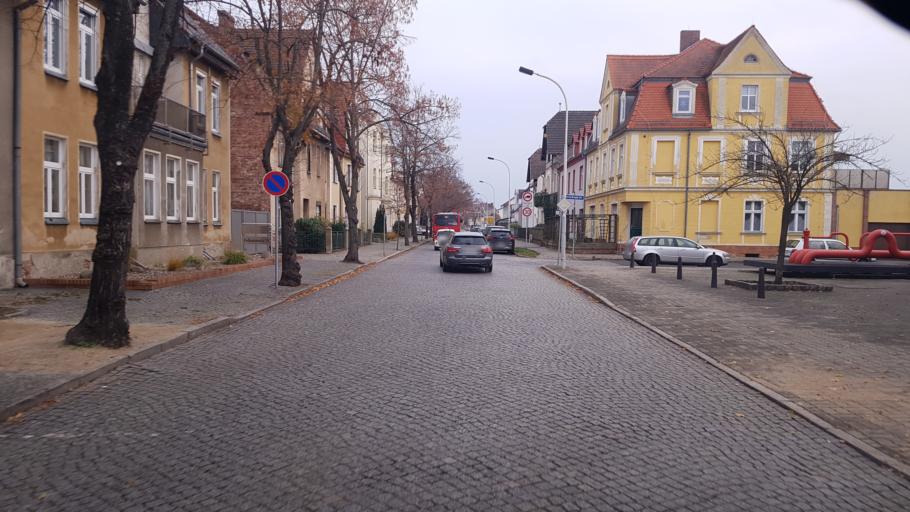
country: DE
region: Brandenburg
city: Eisenhuettenstadt
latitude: 52.1450
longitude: 14.6658
